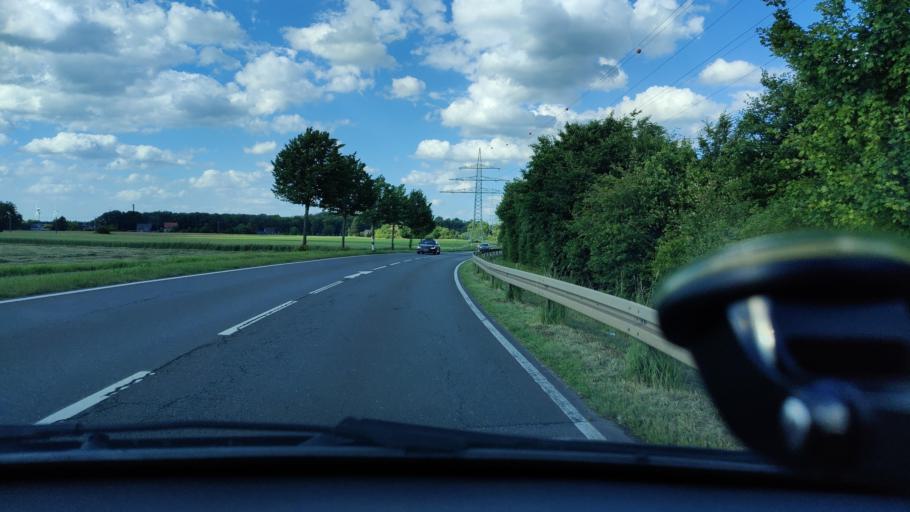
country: DE
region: North Rhine-Westphalia
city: Rheinberg
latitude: 51.5452
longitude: 6.5668
